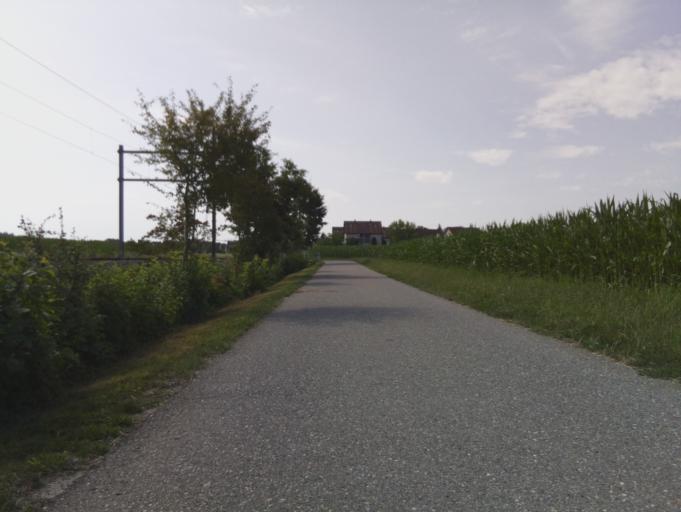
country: CH
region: Zurich
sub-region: Bezirk Andelfingen
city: Henggart
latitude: 47.5693
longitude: 8.6829
